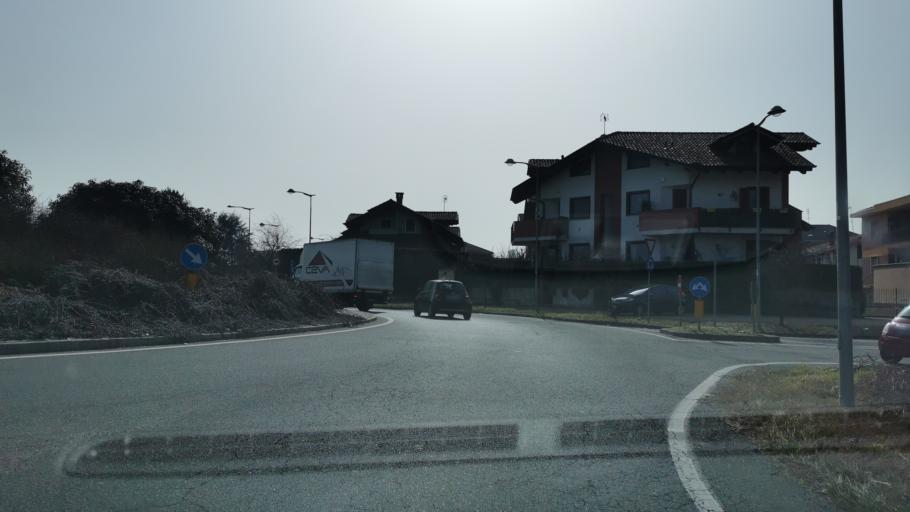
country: IT
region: Piedmont
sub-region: Provincia di Torino
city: Volpiano
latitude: 45.2106
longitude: 7.7735
